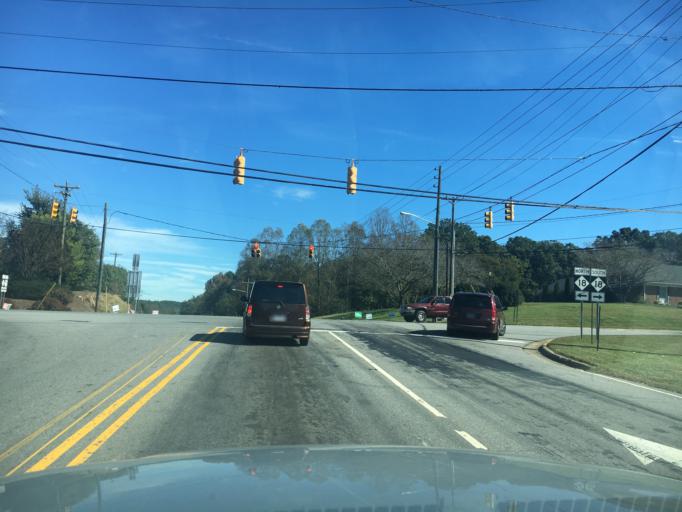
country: US
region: North Carolina
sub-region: Burke County
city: Morganton
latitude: 35.7645
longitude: -81.6909
